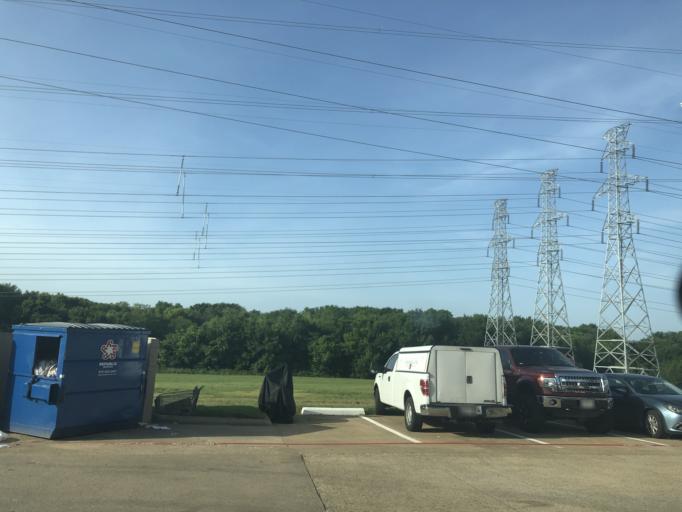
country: US
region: Texas
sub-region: Dallas County
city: Sunnyvale
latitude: 32.8345
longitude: -96.5854
